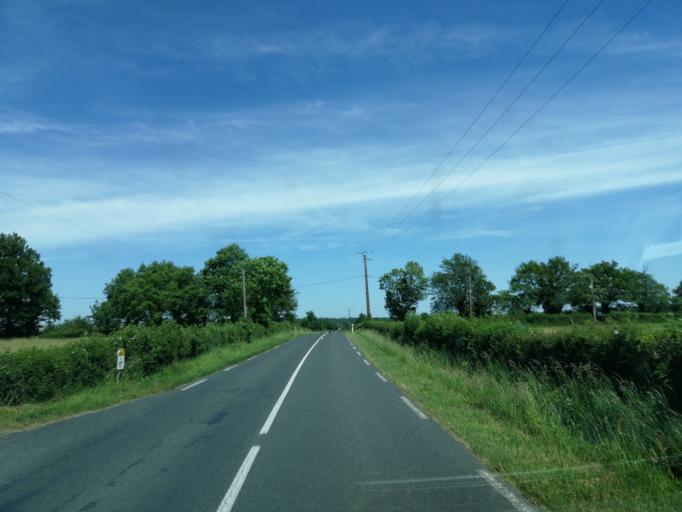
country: FR
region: Poitou-Charentes
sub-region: Departement des Deux-Sevres
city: Bressuire
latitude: 46.8210
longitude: -0.5234
